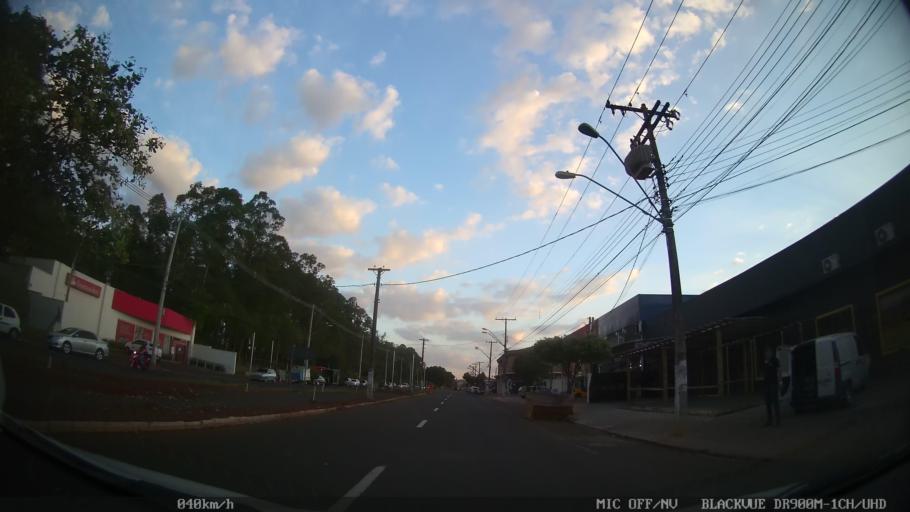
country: BR
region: Sao Paulo
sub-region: Ribeirao Preto
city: Ribeirao Preto
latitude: -21.1563
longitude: -47.7841
